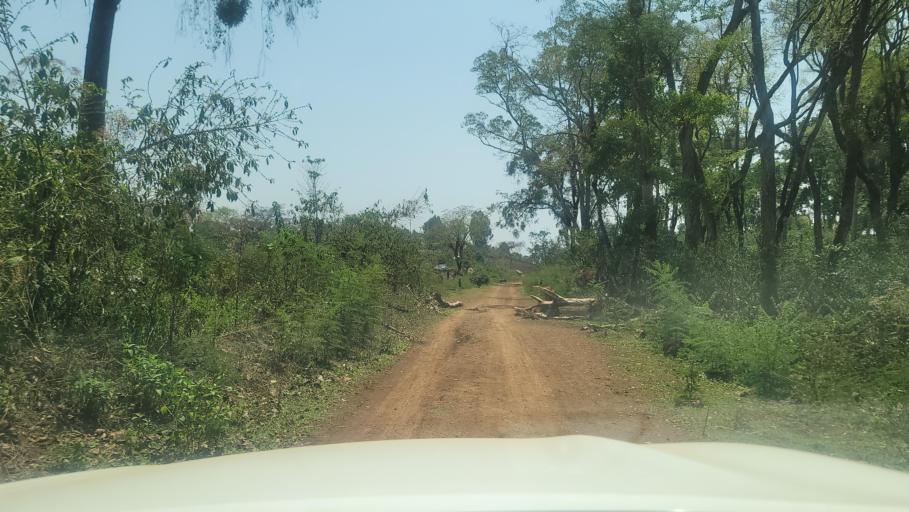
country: ET
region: Southern Nations, Nationalities, and People's Region
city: Bonga
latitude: 7.5336
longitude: 36.1878
